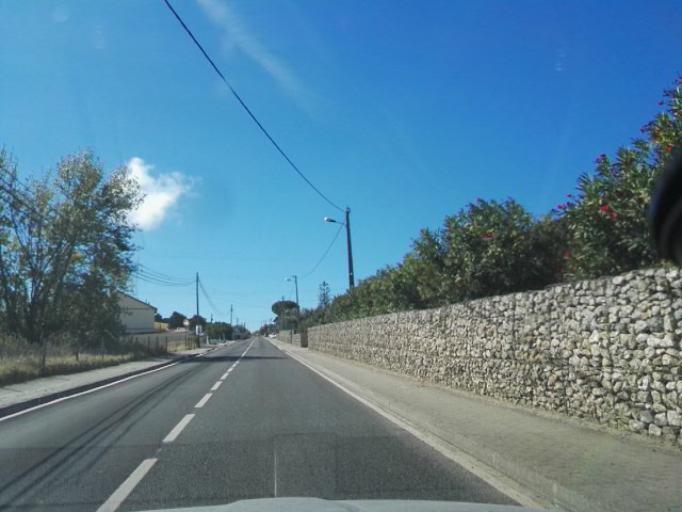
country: PT
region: Lisbon
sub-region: Arruda Dos Vinhos
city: Arruda dos Vinhos
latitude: 38.9578
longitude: -9.0586
